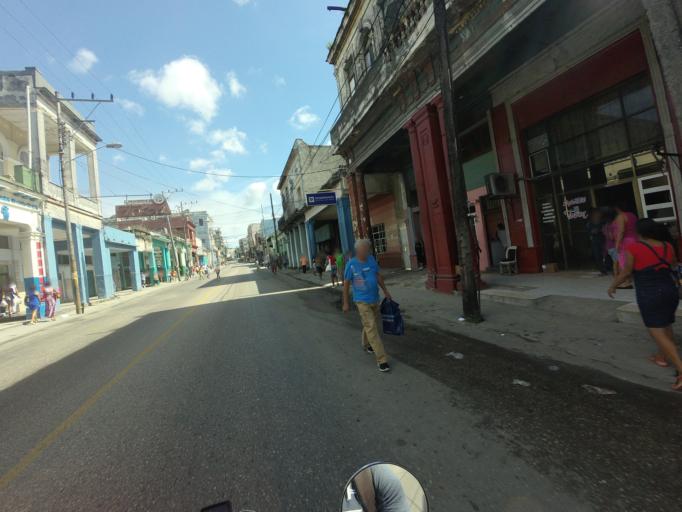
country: CU
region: La Habana
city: Diez de Octubre
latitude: 23.0959
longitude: -82.3634
